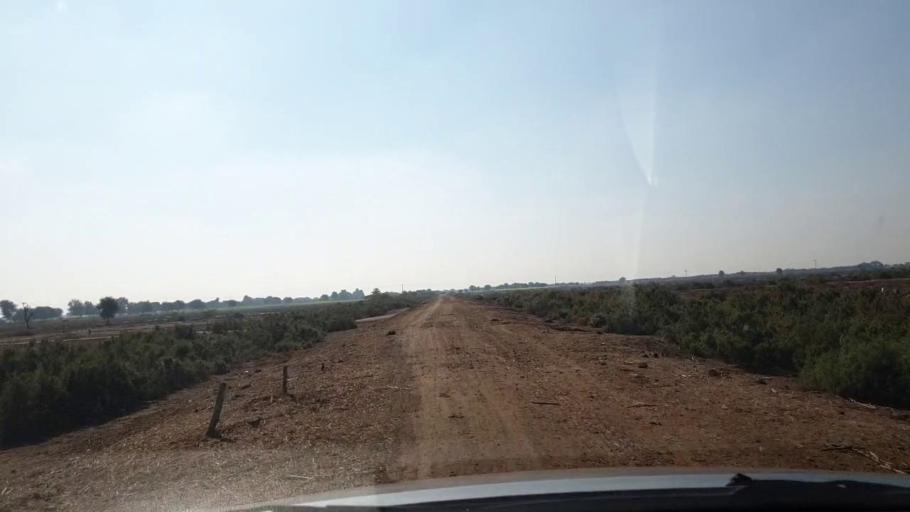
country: PK
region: Sindh
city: Jhol
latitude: 25.8749
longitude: 68.8952
